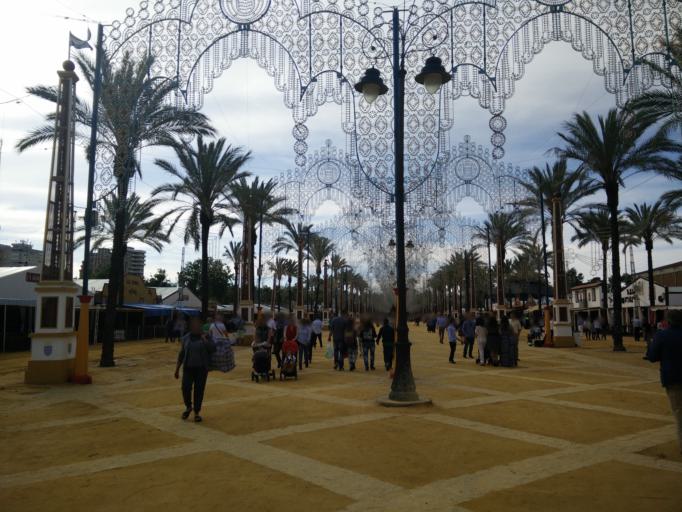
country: ES
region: Andalusia
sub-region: Provincia de Cadiz
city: Jerez de la Frontera
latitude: 36.6938
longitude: -6.1232
